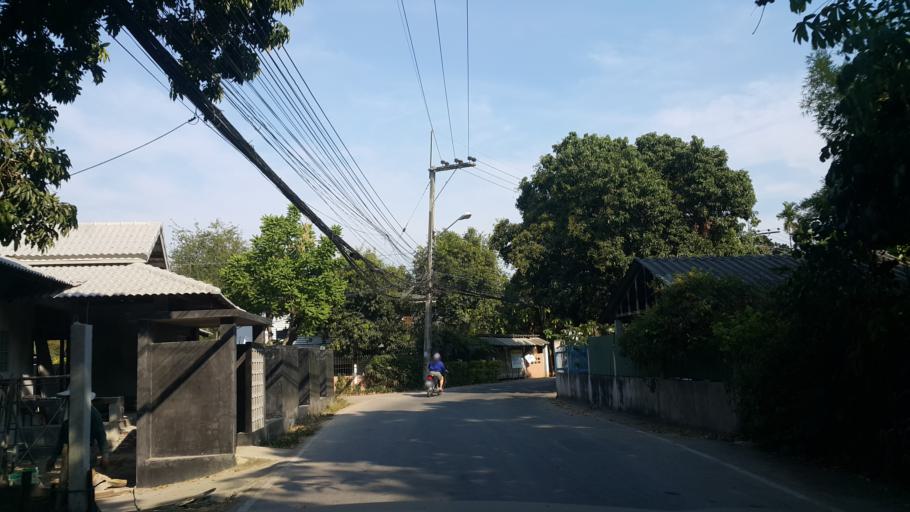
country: TH
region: Chiang Mai
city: San Sai
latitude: 18.8576
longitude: 99.0389
